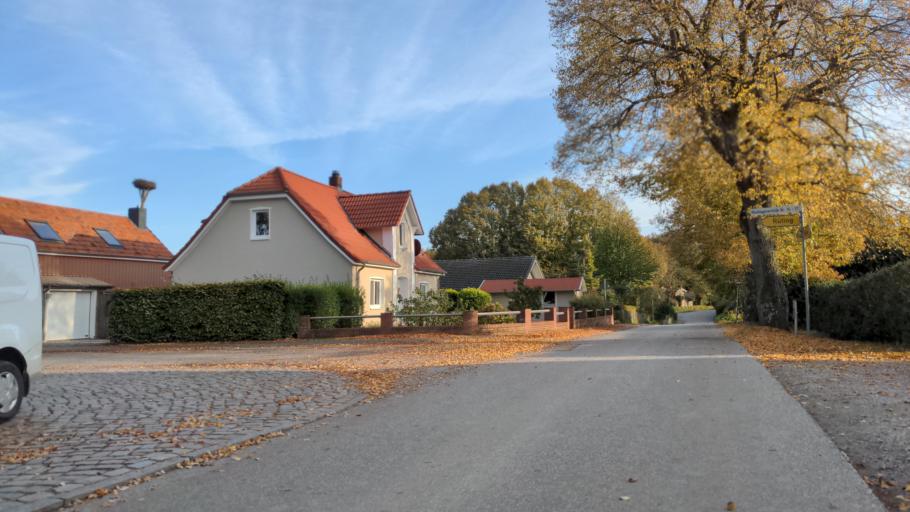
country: DE
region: Schleswig-Holstein
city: Manhagen
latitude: 54.1931
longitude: 10.9401
